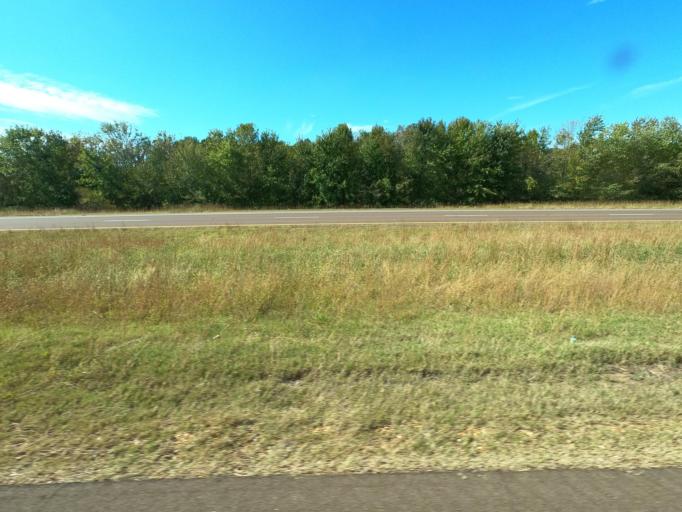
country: US
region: Tennessee
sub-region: Dyer County
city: Dyersburg
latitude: 35.9840
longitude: -89.3426
